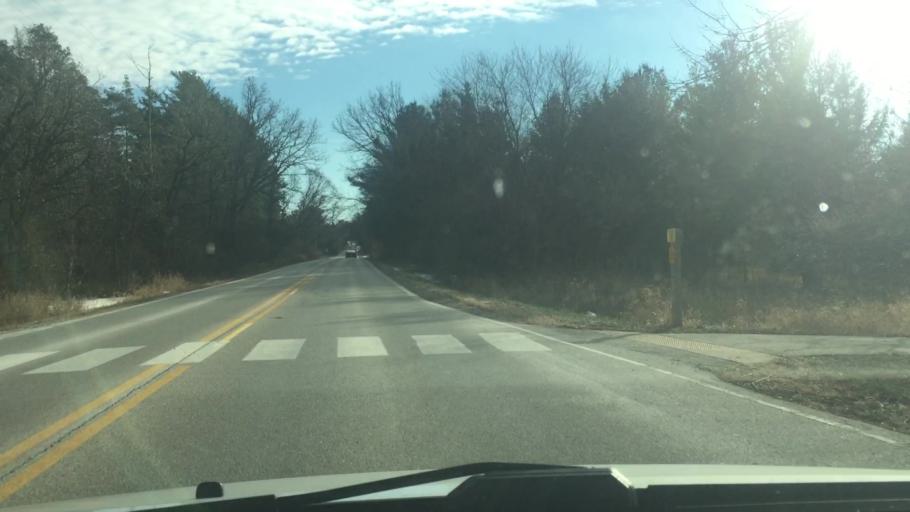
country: US
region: Wisconsin
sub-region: Waukesha County
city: Delafield
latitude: 43.0405
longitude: -88.4043
